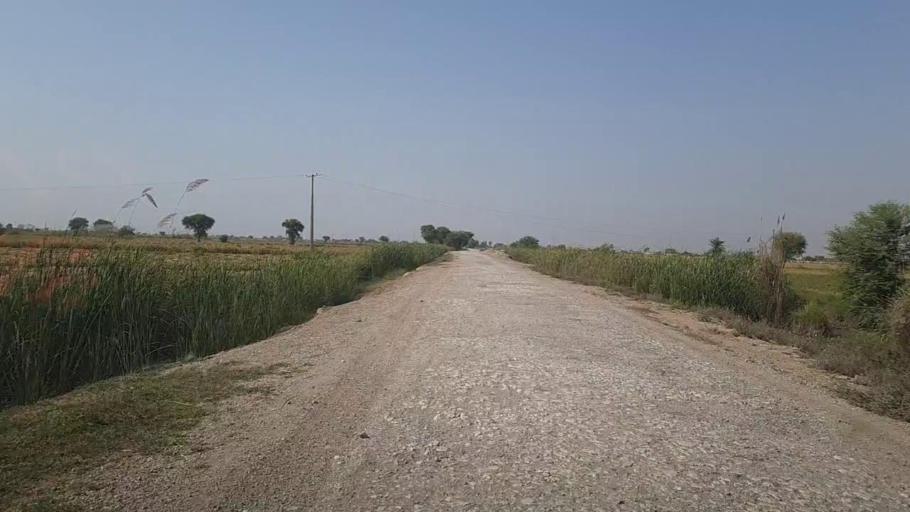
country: PK
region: Sindh
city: Kandhkot
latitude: 28.4004
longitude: 69.2641
